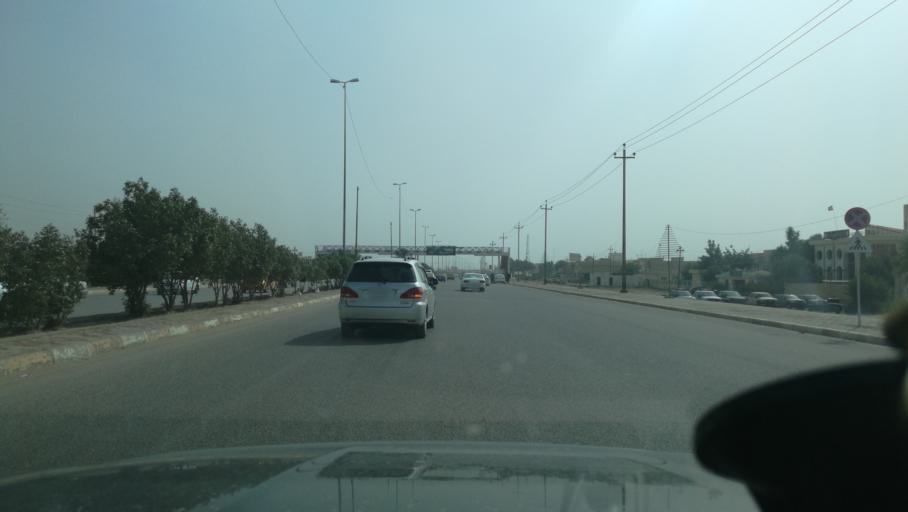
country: IQ
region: Dhi Qar
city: An Nasiriyah
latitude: 31.0678
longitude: 46.2483
